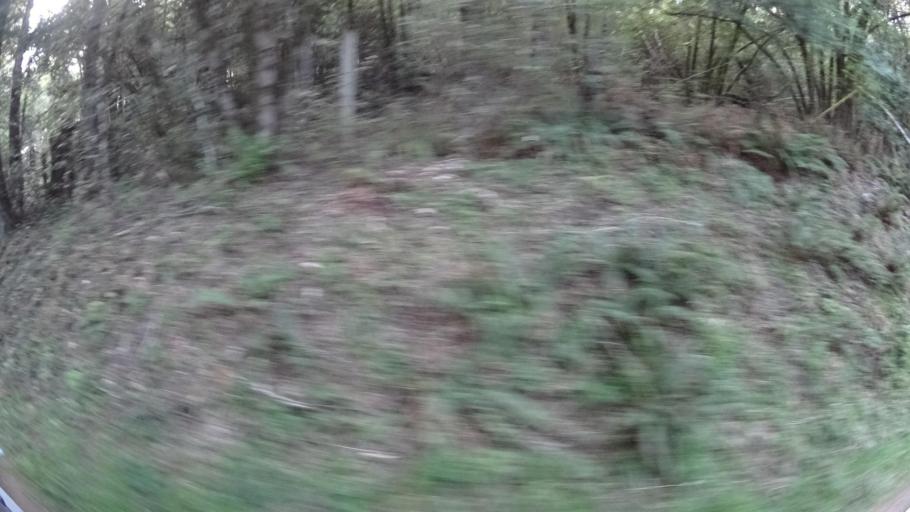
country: US
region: California
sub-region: Humboldt County
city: Blue Lake
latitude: 40.7390
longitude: -123.9535
